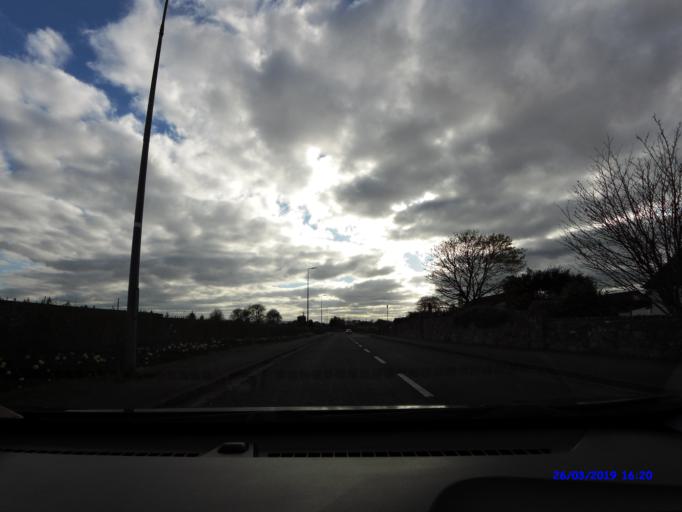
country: IE
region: Connaught
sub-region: Maigh Eo
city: Swinford
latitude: 53.9383
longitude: -8.9556
